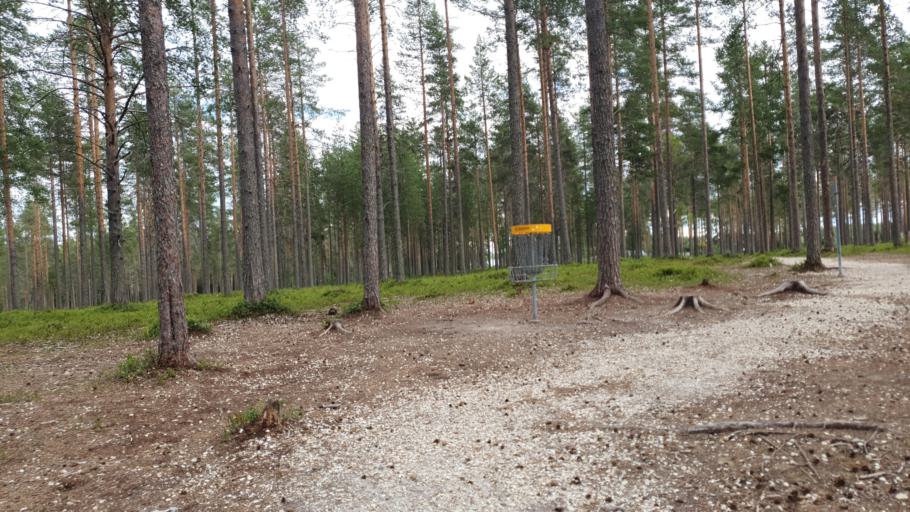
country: FI
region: Kainuu
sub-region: Kehys-Kainuu
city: Kuhmo
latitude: 64.1308
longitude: 29.5380
